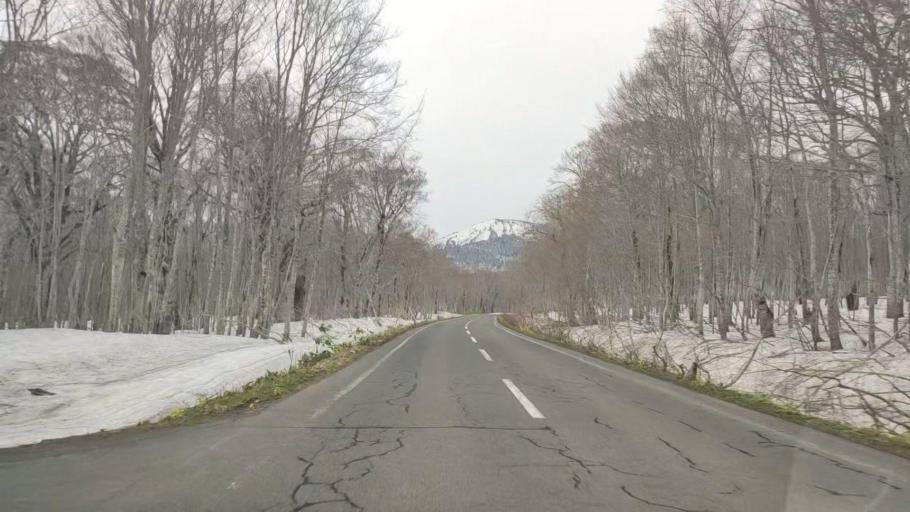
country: JP
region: Aomori
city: Aomori Shi
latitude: 40.6360
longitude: 140.9303
